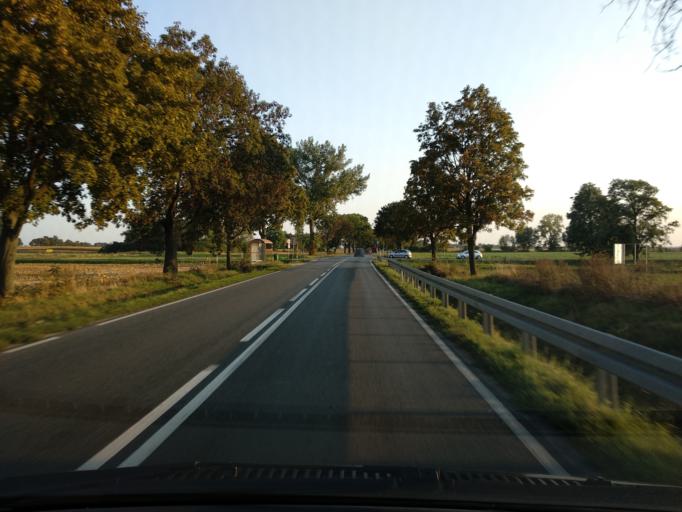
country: PL
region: Lower Silesian Voivodeship
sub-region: Powiat wroclawski
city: Zorawina
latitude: 50.9335
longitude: 17.0693
